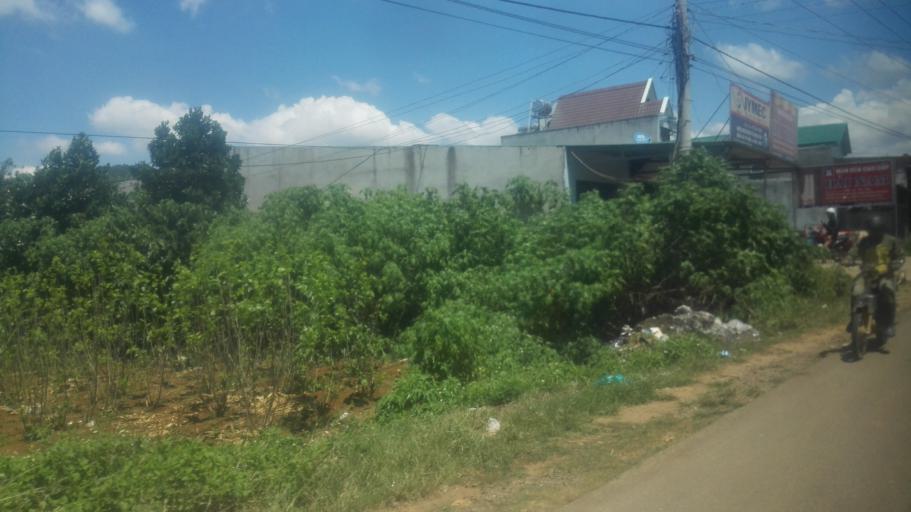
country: VN
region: Lam Dong
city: Da Lat
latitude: 11.8805
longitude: 108.3419
